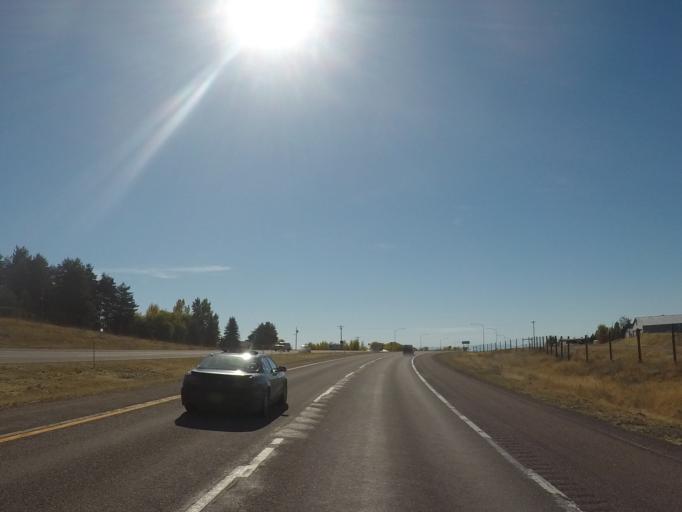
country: US
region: Montana
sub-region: Lake County
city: Polson
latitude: 47.6697
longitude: -114.1069
